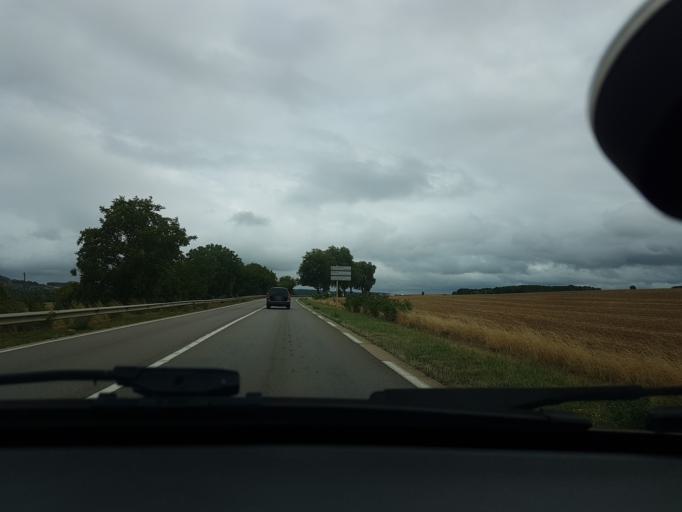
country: FR
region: Bourgogne
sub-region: Departement de l'Yonne
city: Saint-Bris-le-Vineux
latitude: 47.6940
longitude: 3.6425
